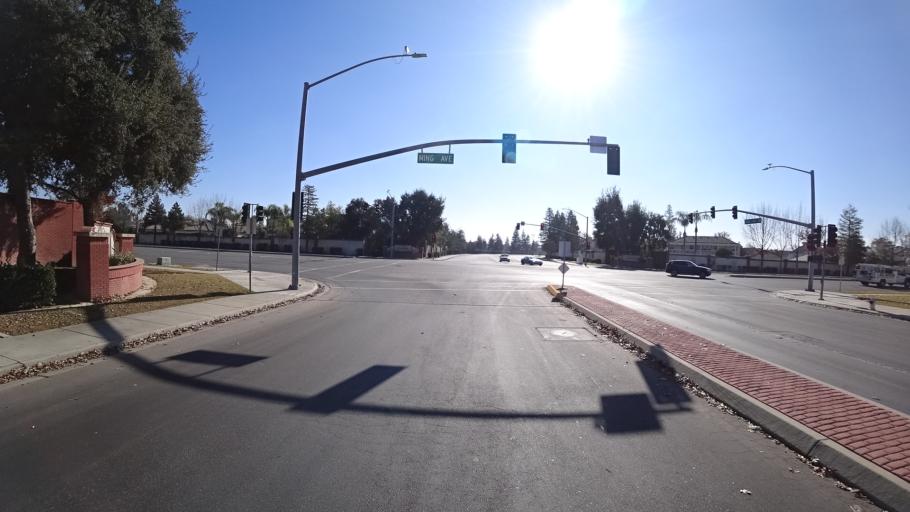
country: US
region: California
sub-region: Kern County
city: Greenacres
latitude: 35.3402
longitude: -119.1212
